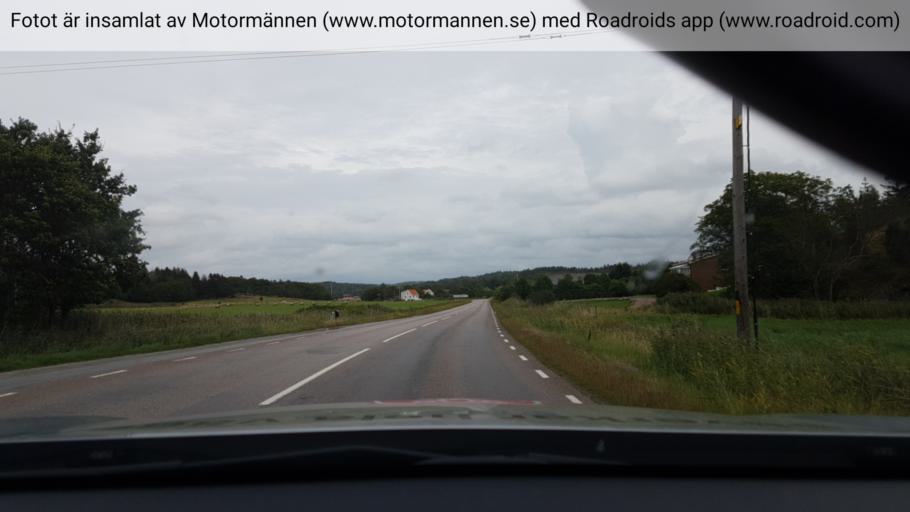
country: SE
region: Vaestra Goetaland
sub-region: Tanums Kommun
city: Grebbestad
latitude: 58.5941
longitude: 11.3168
